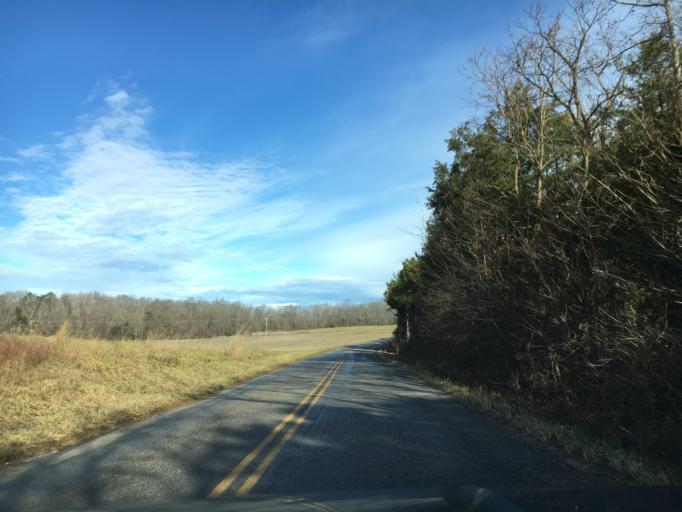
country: US
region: Virginia
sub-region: Nottoway County
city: Crewe
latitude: 37.3200
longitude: -78.1745
